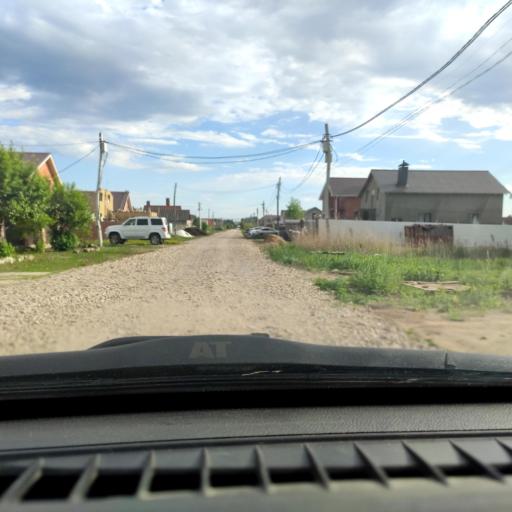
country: RU
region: Samara
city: Tol'yatti
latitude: 53.5657
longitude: 49.4076
